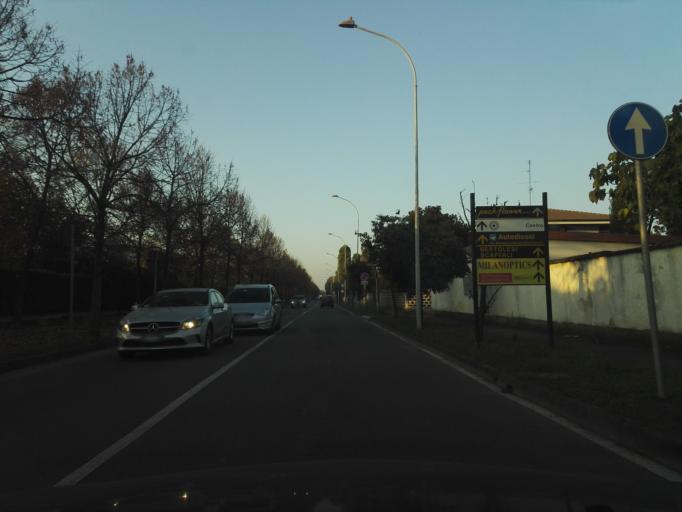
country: IT
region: Lombardy
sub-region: Citta metropolitana di Milano
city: Vigliano-Bettolino
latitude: 45.4319
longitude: 9.3478
